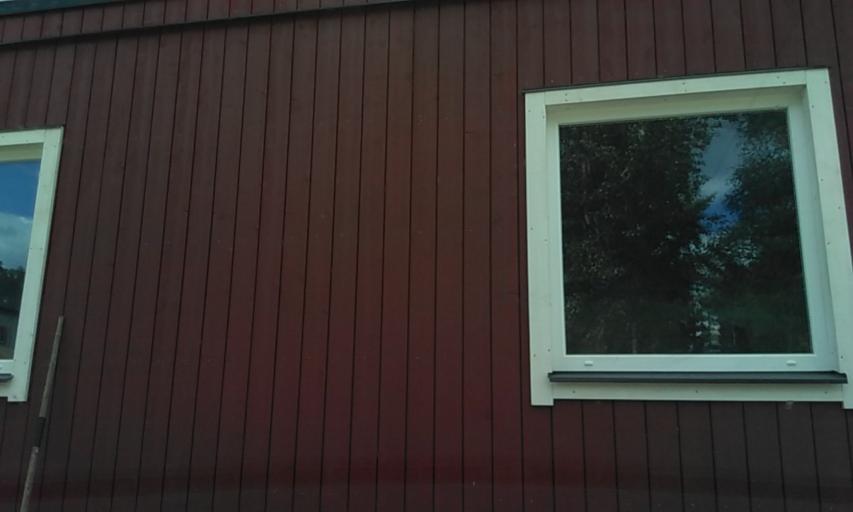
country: SE
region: Vaestra Goetaland
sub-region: Boras Kommun
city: Sjomarken
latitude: 57.7947
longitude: 12.8685
